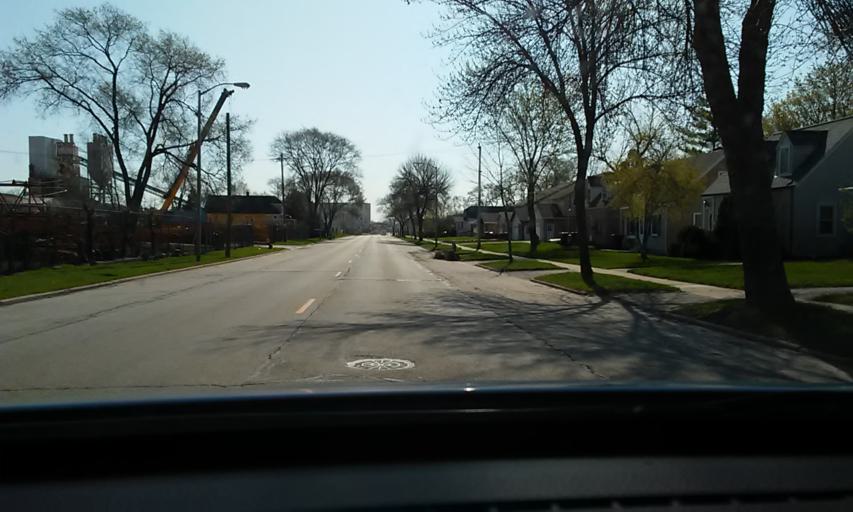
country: US
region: Wisconsin
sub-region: Milwaukee County
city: West Allis
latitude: 43.0239
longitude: -88.0217
